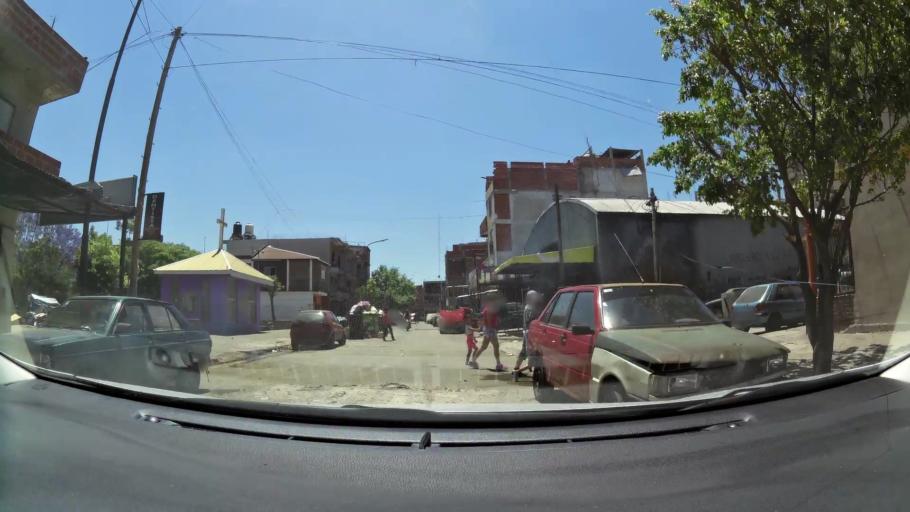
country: AR
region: Buenos Aires
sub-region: Partido de Avellaneda
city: Avellaneda
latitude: -34.6553
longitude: -58.4014
